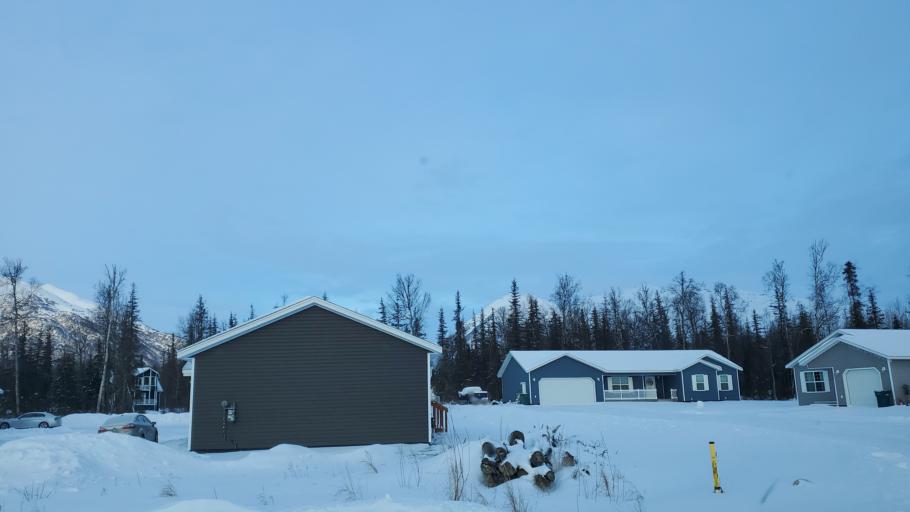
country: US
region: Alaska
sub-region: Matanuska-Susitna Borough
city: Fishhook
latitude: 61.6833
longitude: -149.2419
